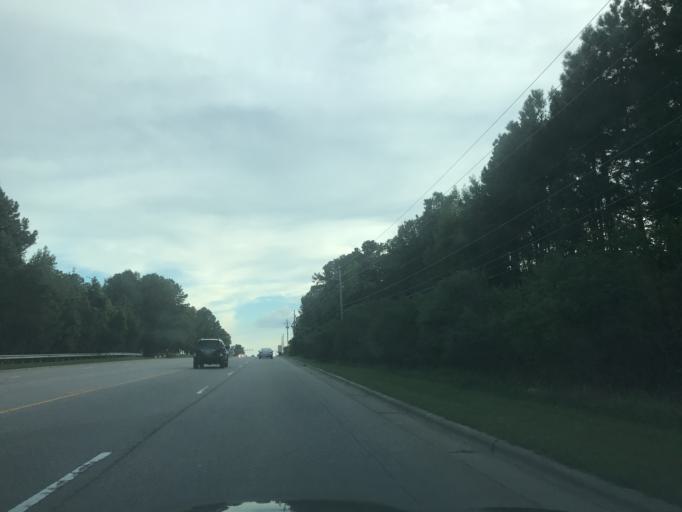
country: US
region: North Carolina
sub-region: Wake County
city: Green Level
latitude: 35.7648
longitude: -78.8750
